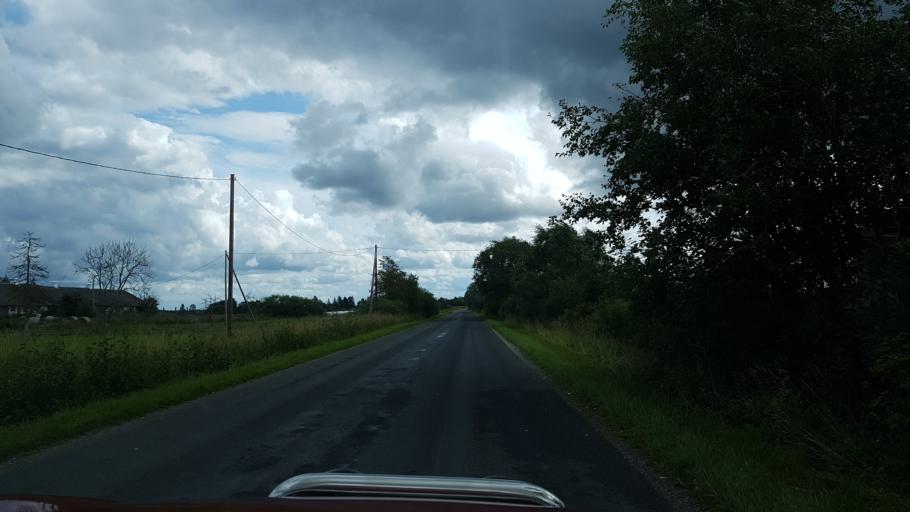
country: EE
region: Laeaene
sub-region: Lihula vald
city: Lihula
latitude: 58.7178
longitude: 23.9868
